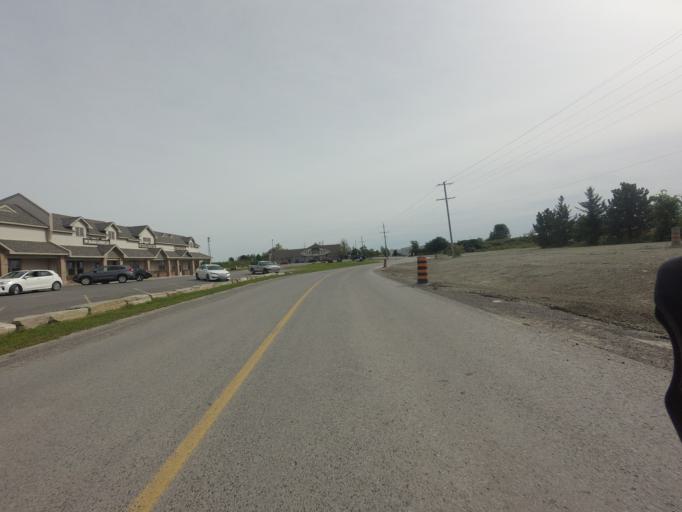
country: CA
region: Ontario
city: Carleton Place
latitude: 45.1441
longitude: -76.1294
